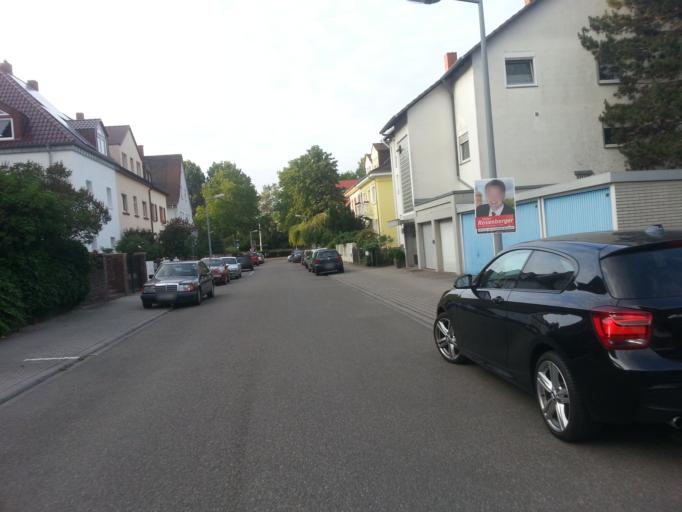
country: DE
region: Baden-Wuerttemberg
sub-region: Karlsruhe Region
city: Mannheim
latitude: 49.4814
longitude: 8.5078
